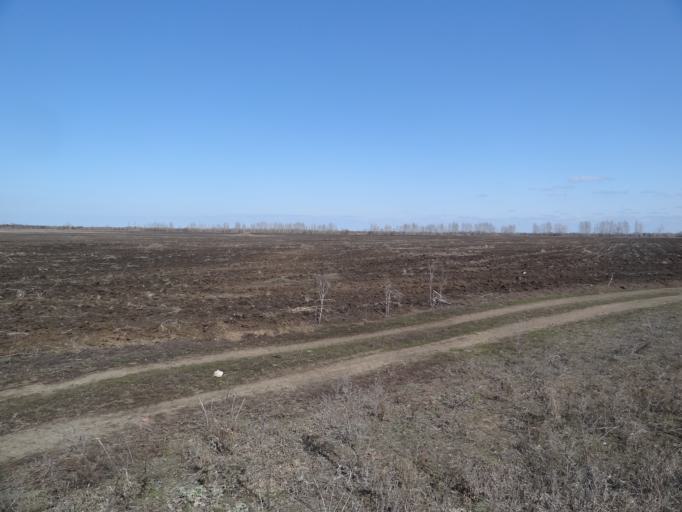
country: RU
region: Saratov
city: Shumeyka
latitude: 51.4102
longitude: 46.2447
